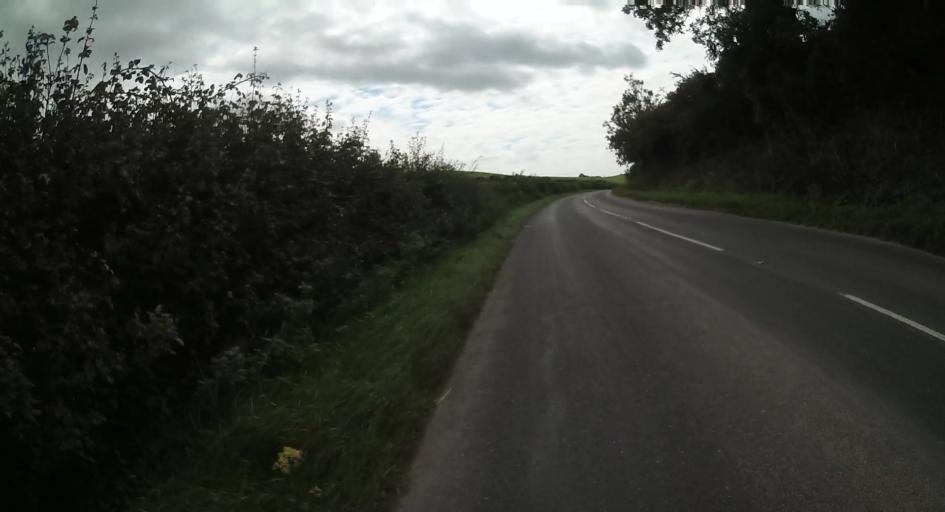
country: GB
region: England
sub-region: Isle of Wight
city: Newport
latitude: 50.6656
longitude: -1.3445
